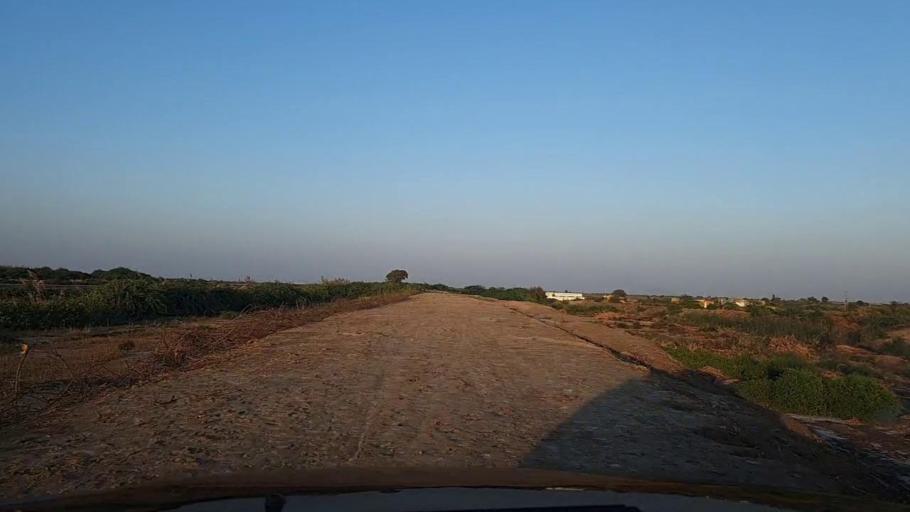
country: PK
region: Sindh
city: Thatta
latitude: 24.7246
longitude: 67.9471
